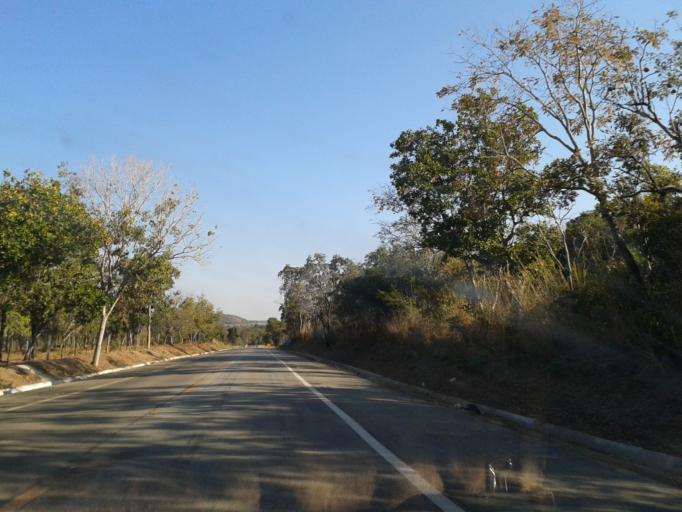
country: BR
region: Goias
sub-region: Itapirapua
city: Itapirapua
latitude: -15.3190
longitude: -50.4381
